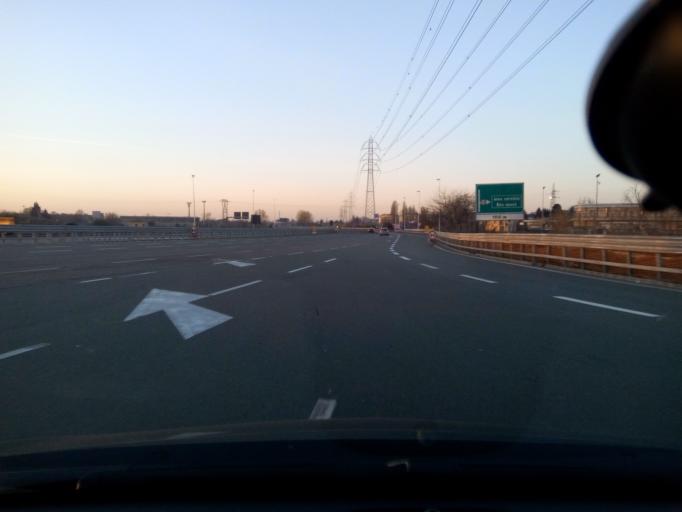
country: IT
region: Lombardy
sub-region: Citta metropolitana di Milano
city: Rho
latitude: 45.5402
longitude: 9.0581
